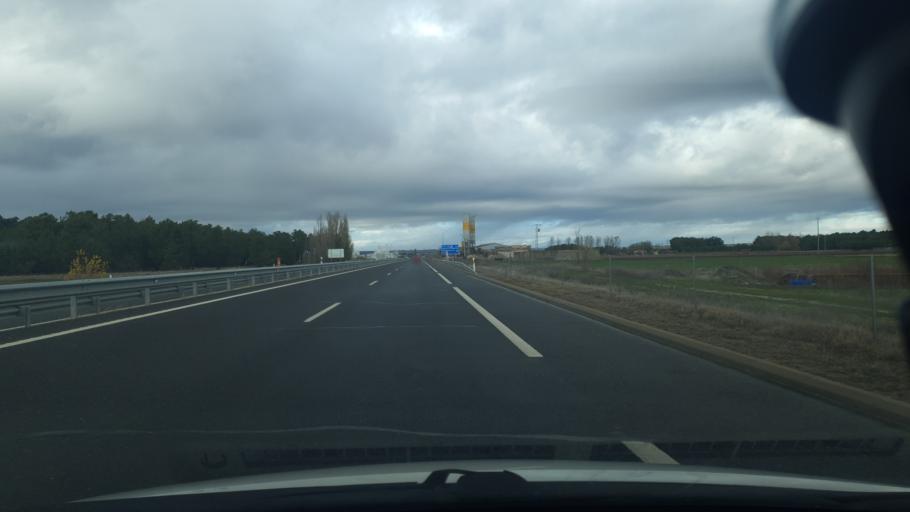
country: ES
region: Castille and Leon
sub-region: Provincia de Segovia
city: Sanchonuno
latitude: 41.3045
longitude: -4.3022
